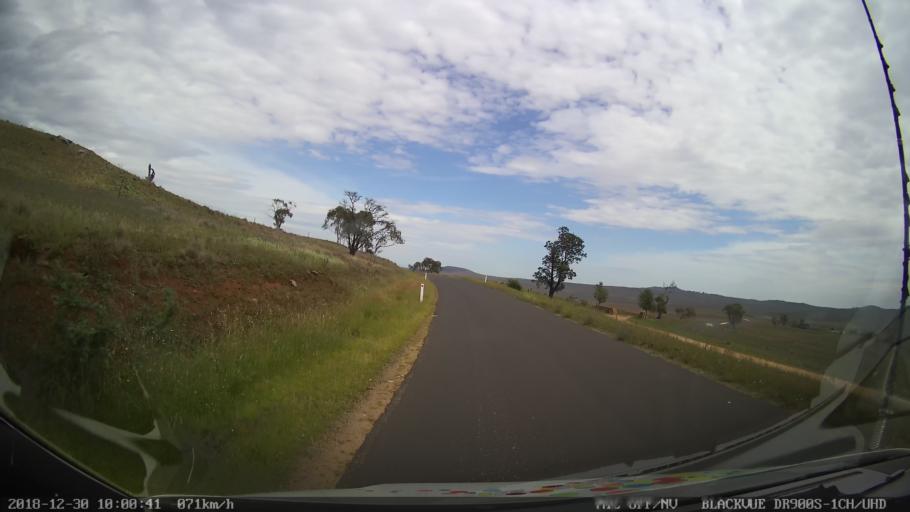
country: AU
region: New South Wales
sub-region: Cooma-Monaro
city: Cooma
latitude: -36.5144
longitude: 149.1963
